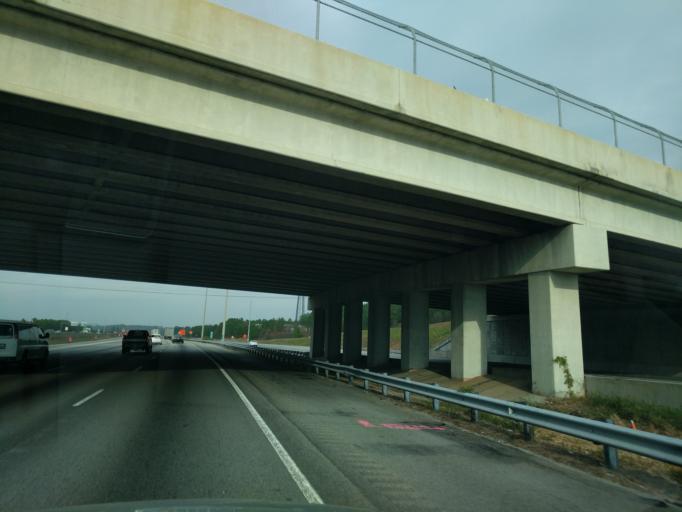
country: US
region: Georgia
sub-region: Gwinnett County
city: Suwanee
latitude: 33.9988
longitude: -84.0758
